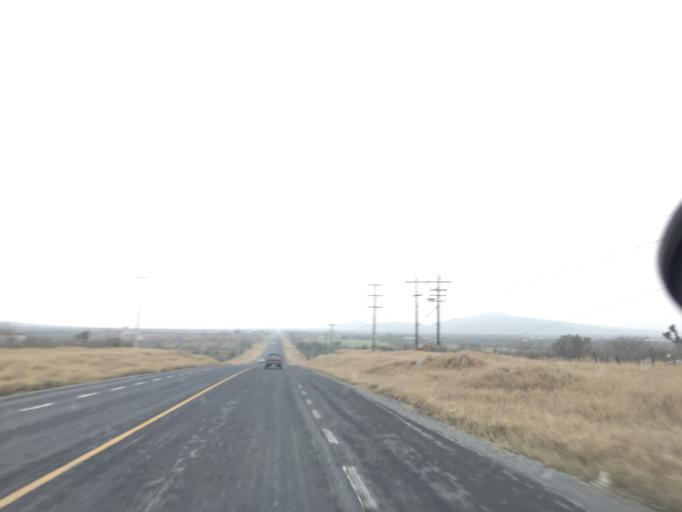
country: MX
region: Nuevo Leon
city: Mina
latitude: 25.9987
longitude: -100.4741
